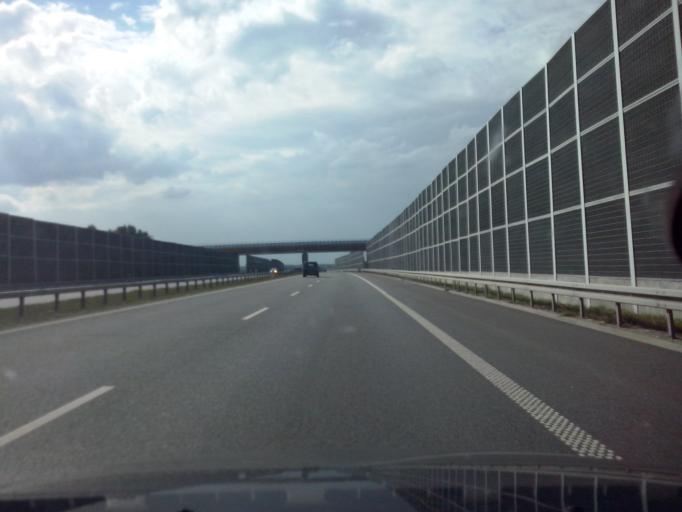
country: PL
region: Lesser Poland Voivodeship
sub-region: Powiat brzeski
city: Debno
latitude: 50.0077
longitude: 20.7529
